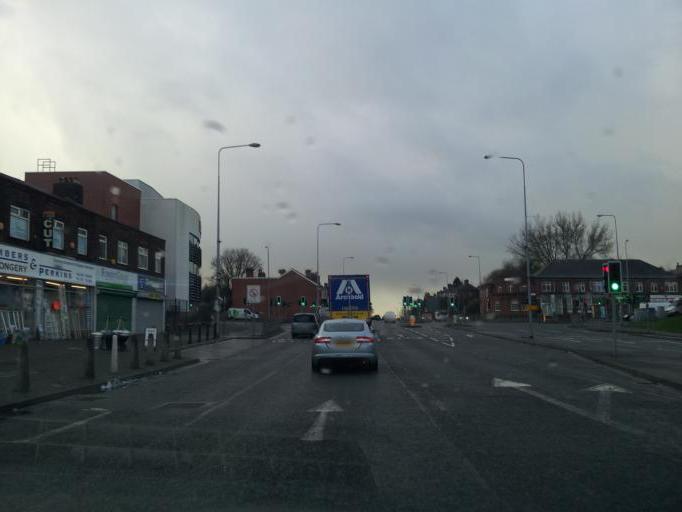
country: GB
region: England
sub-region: Manchester
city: Blackley
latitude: 53.5331
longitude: -2.2076
